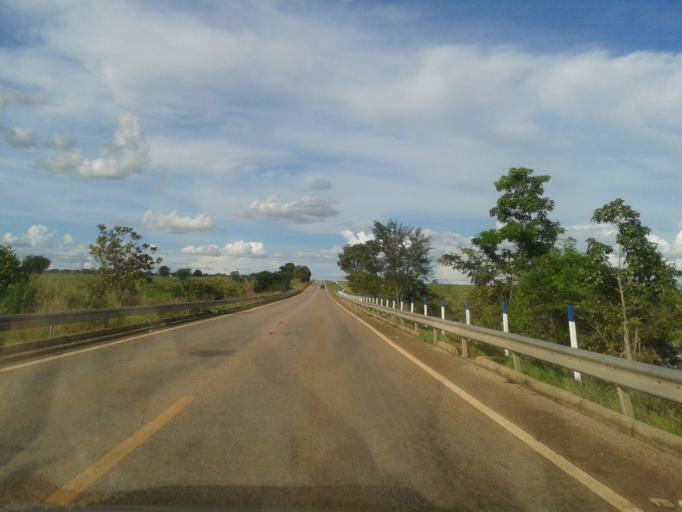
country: BR
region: Goias
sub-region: Mozarlandia
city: Mozarlandia
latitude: -14.3449
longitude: -50.4200
